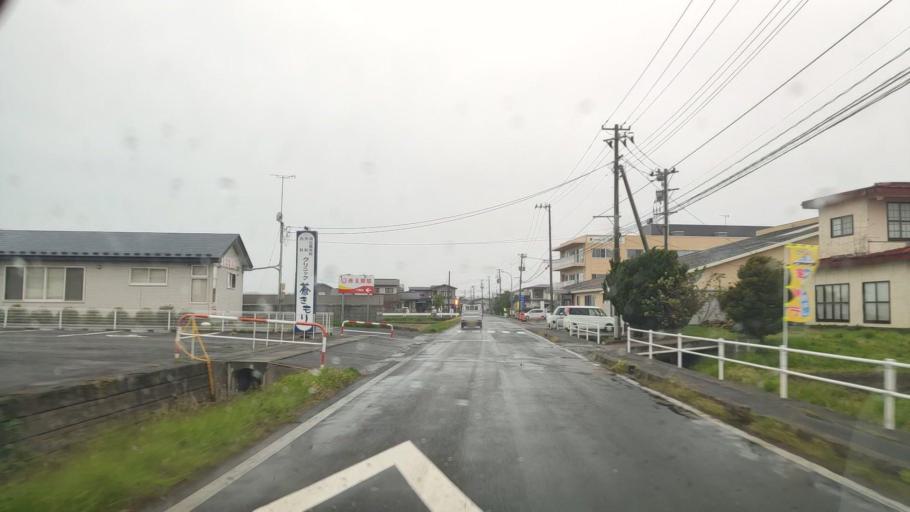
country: JP
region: Akita
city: Noshiromachi
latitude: 40.1027
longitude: 139.9993
